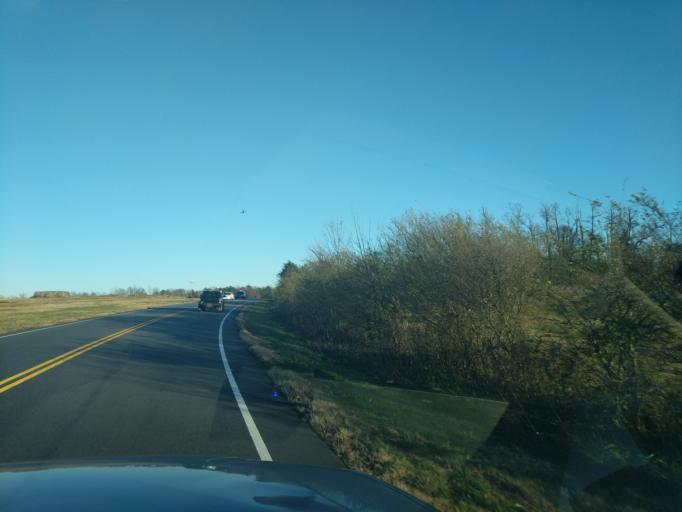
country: US
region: South Carolina
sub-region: Oconee County
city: Utica
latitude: 34.5849
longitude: -82.9274
